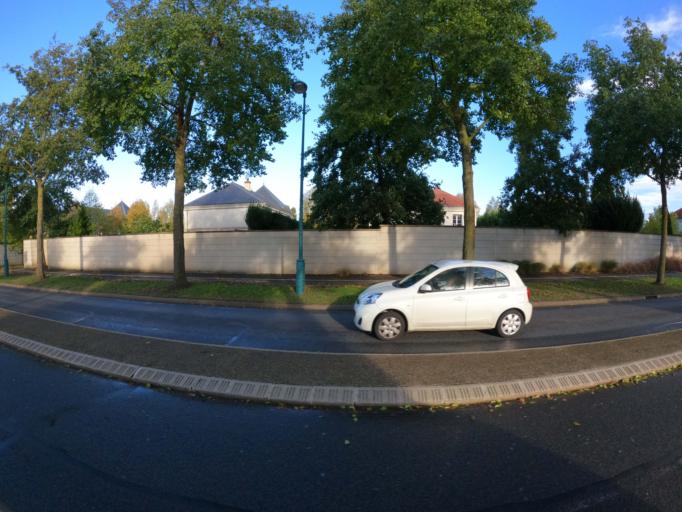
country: FR
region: Ile-de-France
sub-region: Departement de Seine-et-Marne
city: Bailly-Romainvilliers
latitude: 48.8499
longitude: 2.8151
